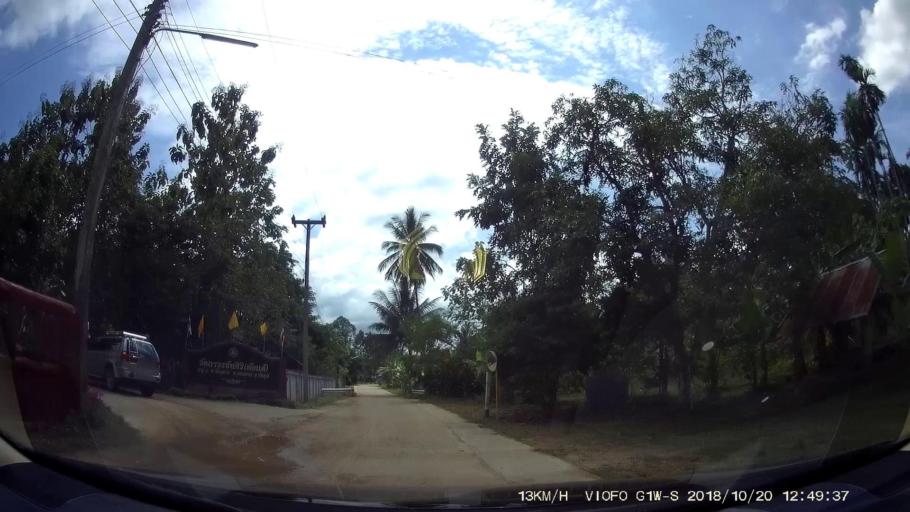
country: TH
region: Chaiyaphum
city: Khon San
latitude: 16.5348
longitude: 101.8936
